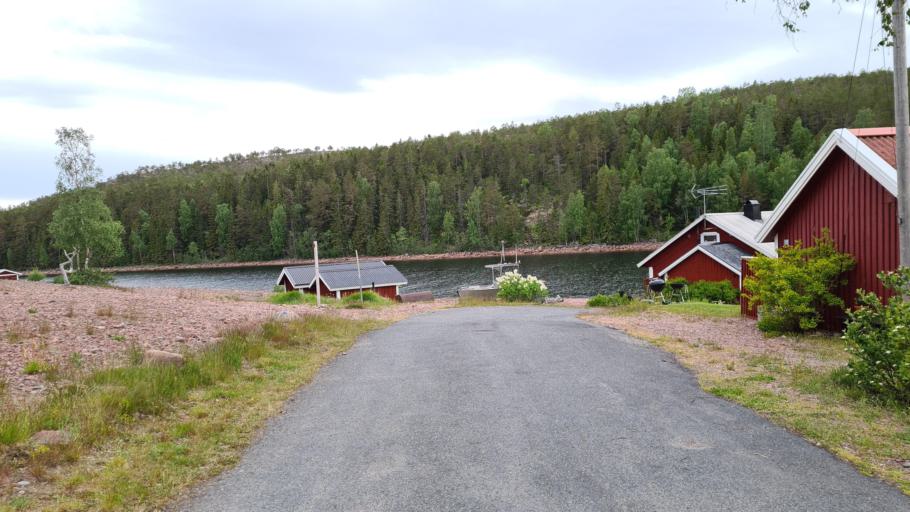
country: SE
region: Vaesternorrland
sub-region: OErnskoeldsviks Kommun
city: Kopmanholmen
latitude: 62.9721
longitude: 18.5201
